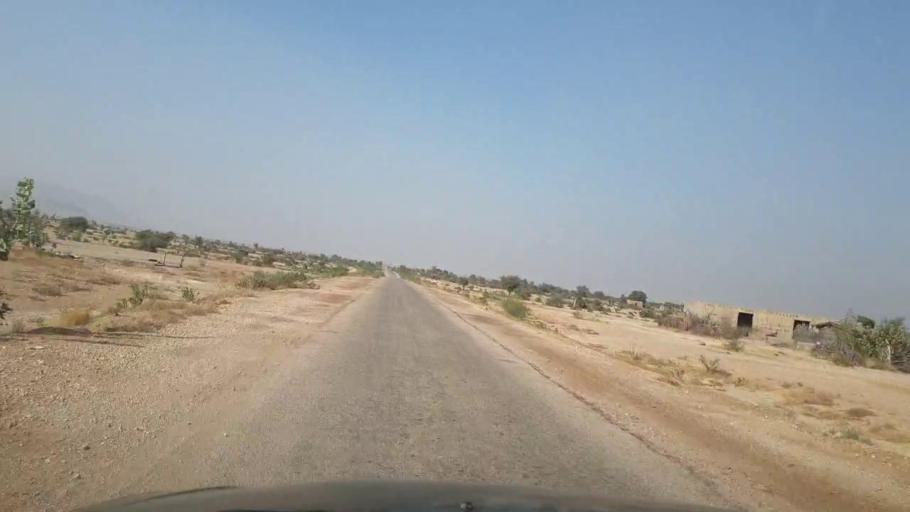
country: PK
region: Sindh
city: Jamshoro
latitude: 25.5842
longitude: 67.8205
